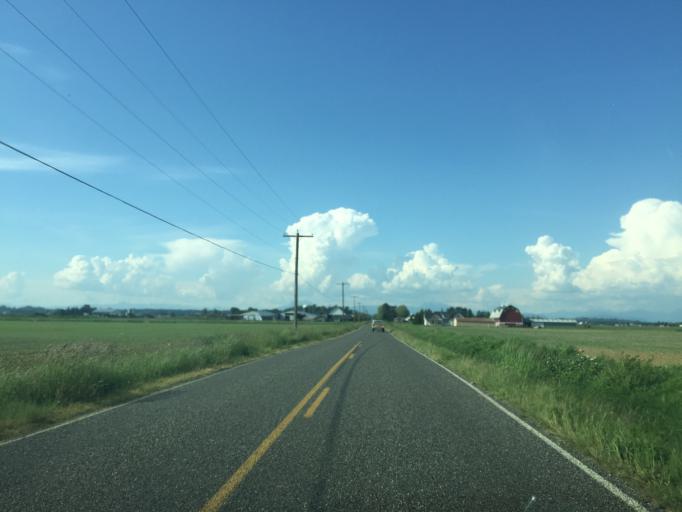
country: US
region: Washington
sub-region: Whatcom County
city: Lynden
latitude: 48.9655
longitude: -122.4411
